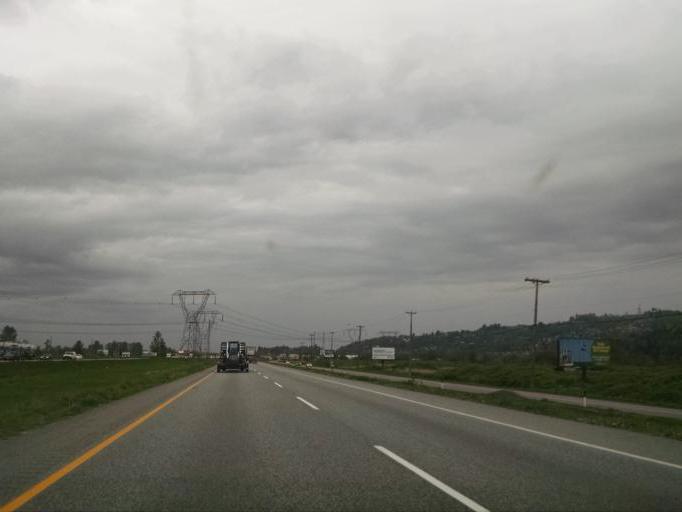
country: CA
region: British Columbia
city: Abbotsford
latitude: 49.0540
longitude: -122.1870
